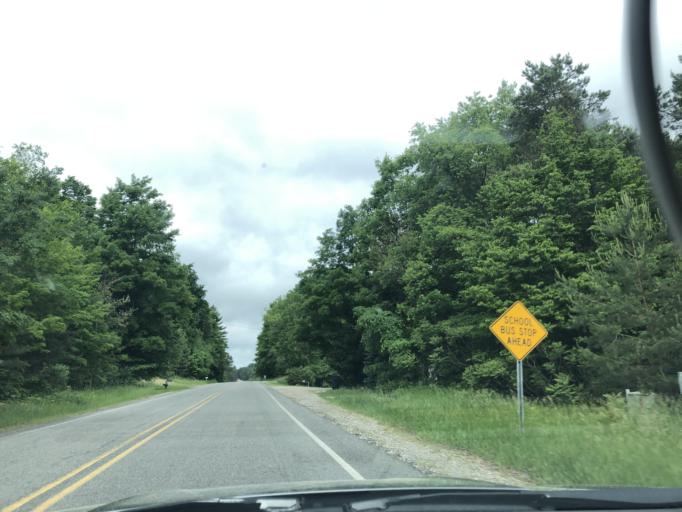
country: US
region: Michigan
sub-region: Missaukee County
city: Lake City
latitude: 44.4537
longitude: -85.2035
